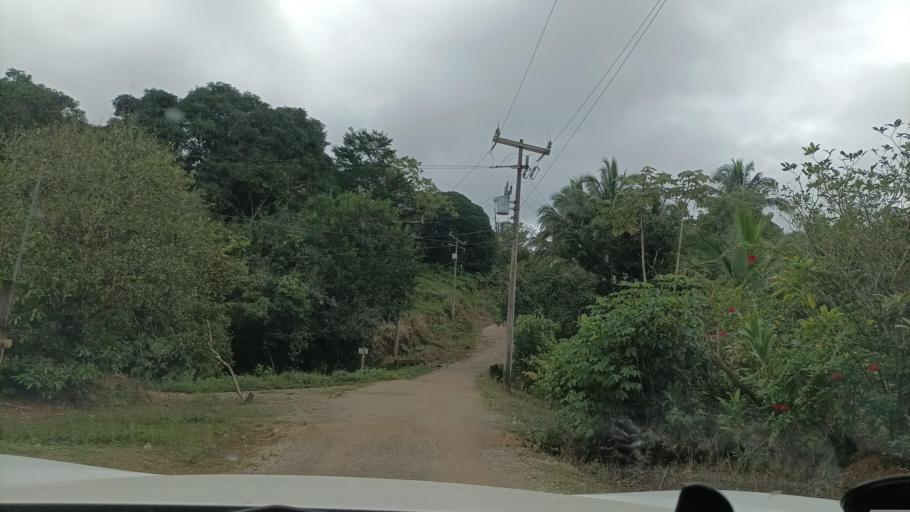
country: MX
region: Veracruz
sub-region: Uxpanapa
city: Poblado 10
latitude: 17.4279
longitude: -94.4209
